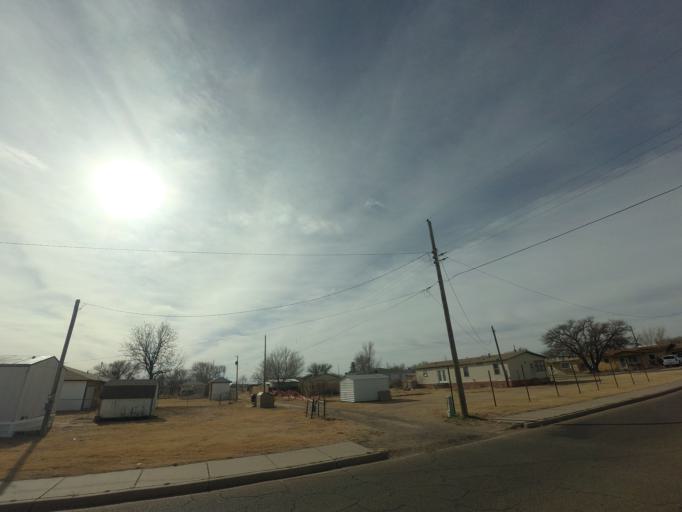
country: US
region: New Mexico
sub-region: Curry County
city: Clovis
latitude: 34.4099
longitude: -103.2357
